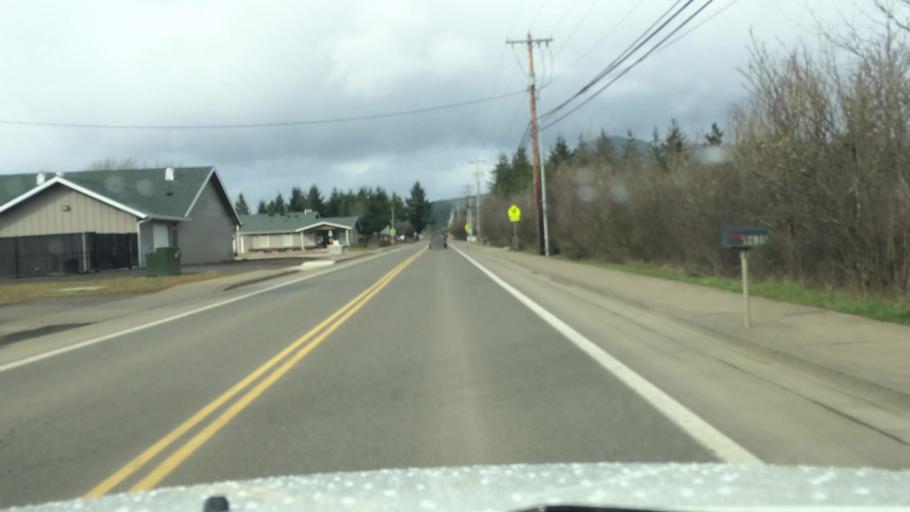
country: US
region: Oregon
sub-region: Polk County
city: Grand Ronde
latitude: 45.0746
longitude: -123.6119
